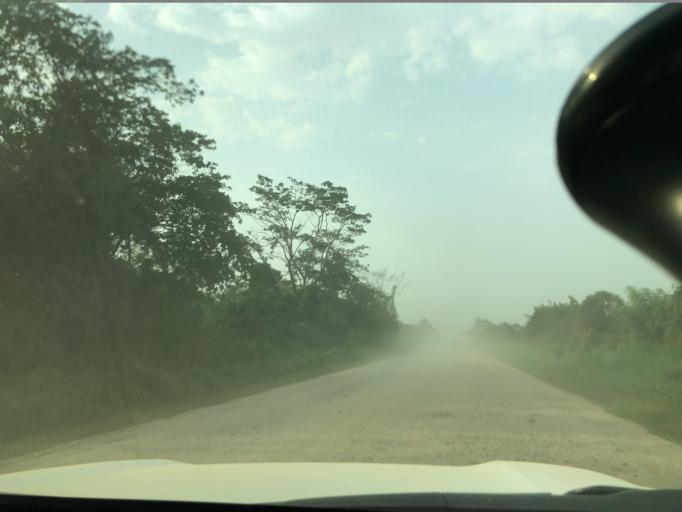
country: UG
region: Western Region
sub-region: Kasese District
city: Margherita
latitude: 0.2679
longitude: 29.6754
